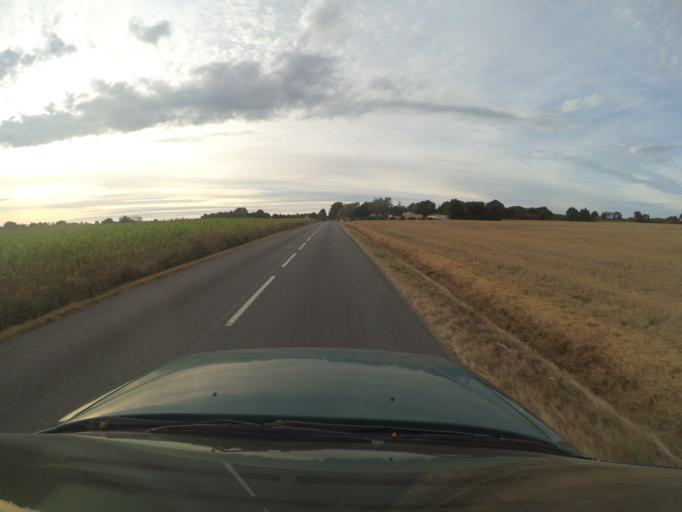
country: FR
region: Pays de la Loire
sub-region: Departement de la Vendee
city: Saint-Andre-Treize-Voies
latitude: 46.8991
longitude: -1.4310
